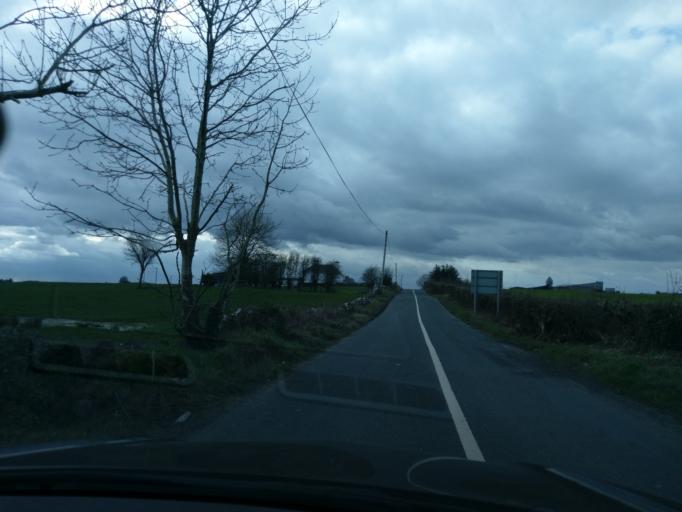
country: IE
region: Connaught
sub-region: County Galway
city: Athenry
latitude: 53.4884
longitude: -8.5843
